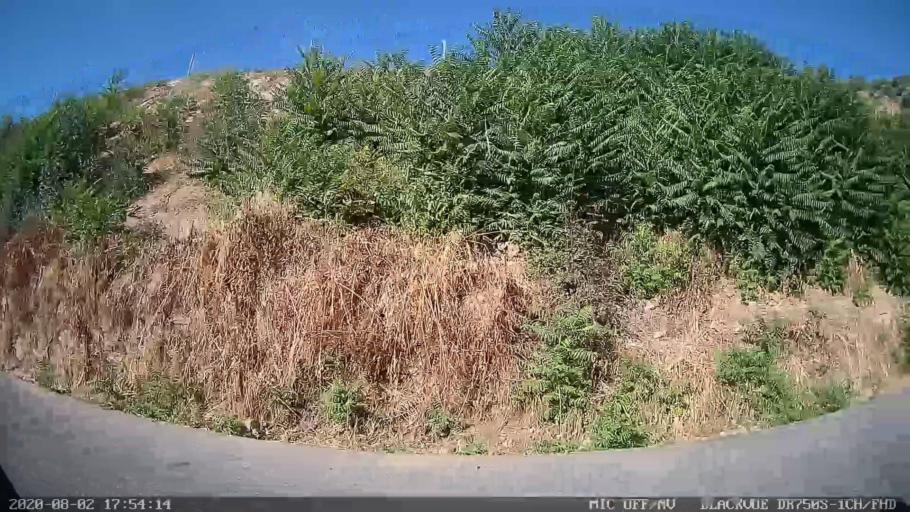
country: PT
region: Vila Real
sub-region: Murca
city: Murca
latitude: 41.4091
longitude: -7.4662
